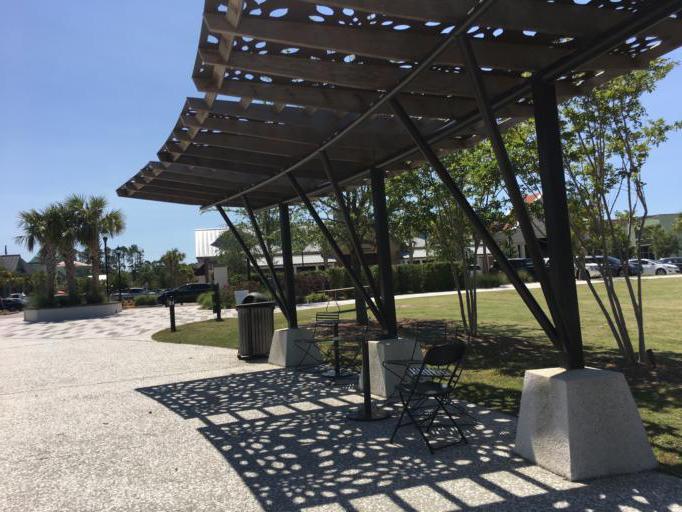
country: US
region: South Carolina
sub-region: Beaufort County
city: Hilton Head Island
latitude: 32.1861
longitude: -80.7222
